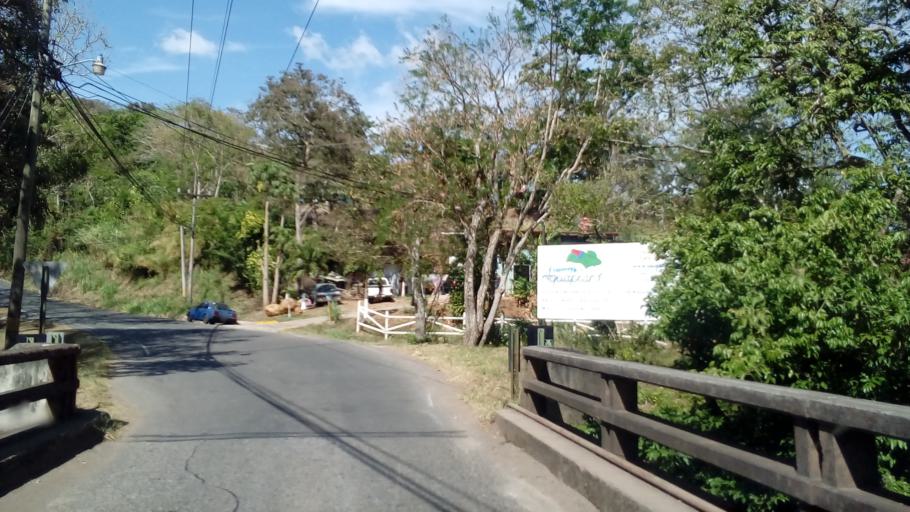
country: CR
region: Guanacaste
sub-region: Canton de Tilaran
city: Tilaran
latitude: 10.4773
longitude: -84.9628
